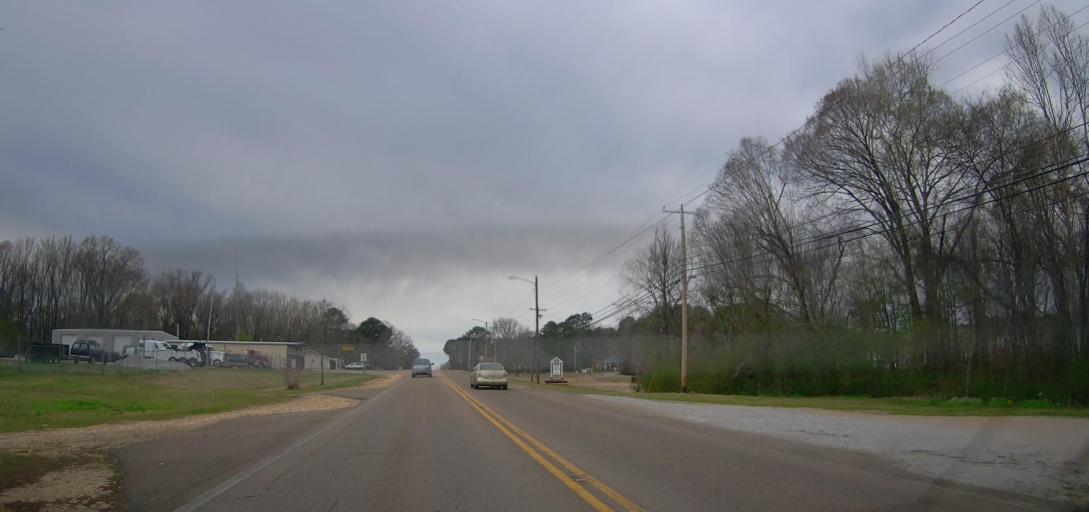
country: US
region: Mississippi
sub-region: Lee County
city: Tupelo
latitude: 34.2578
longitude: -88.6650
